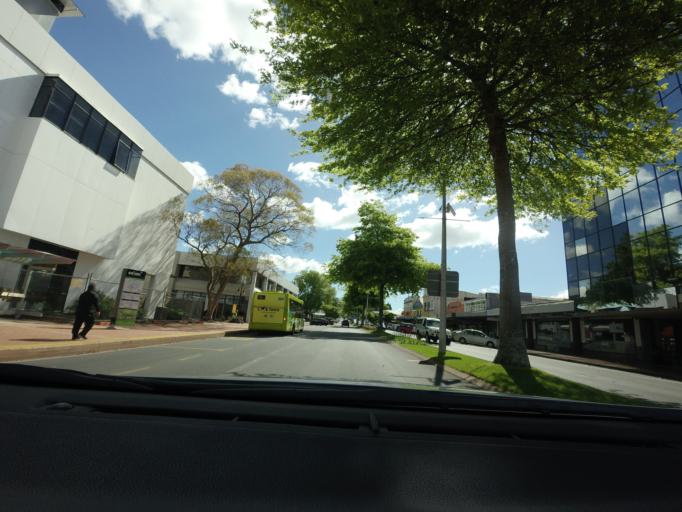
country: NZ
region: Bay of Plenty
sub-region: Rotorua District
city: Rotorua
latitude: -38.1349
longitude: 176.2527
